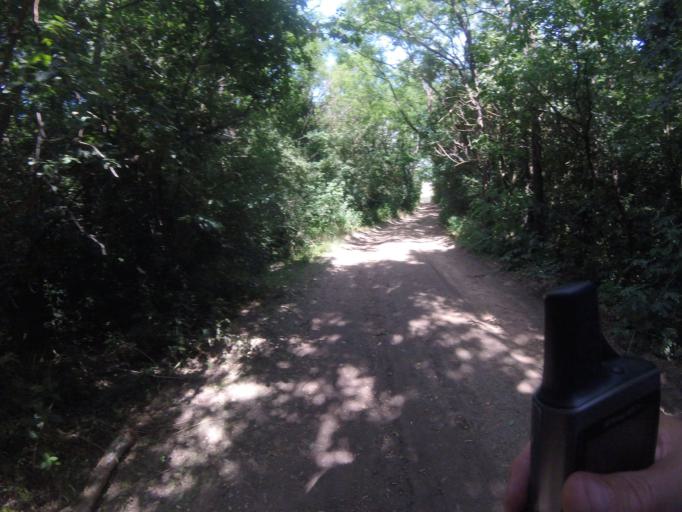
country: HU
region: Fejer
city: Szarliget
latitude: 47.4848
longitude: 18.5002
